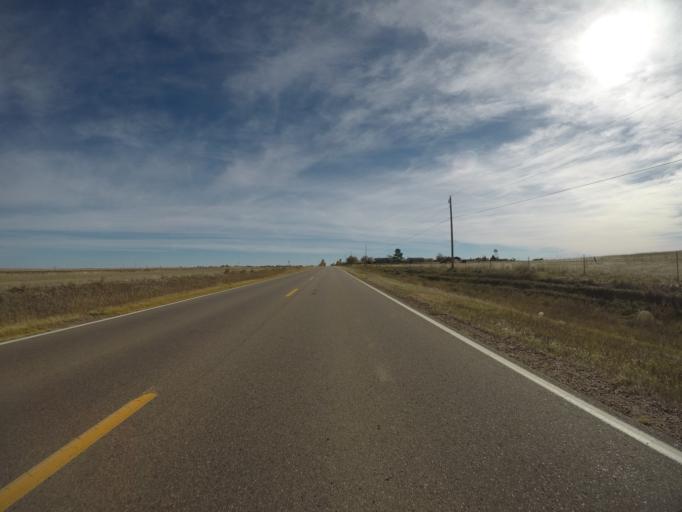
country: US
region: Colorado
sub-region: Adams County
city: Bennett
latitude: 39.7561
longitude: -104.4483
